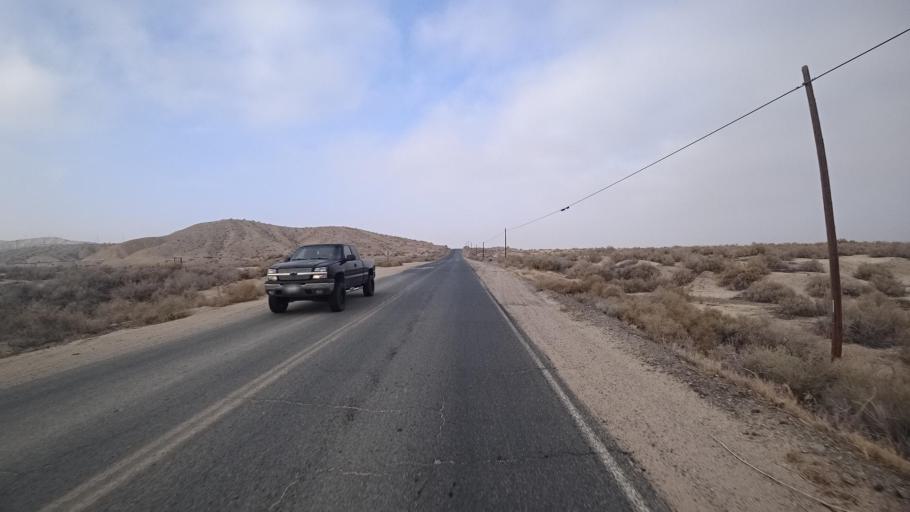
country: US
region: California
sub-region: Kern County
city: Ford City
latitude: 35.1887
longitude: -119.4460
